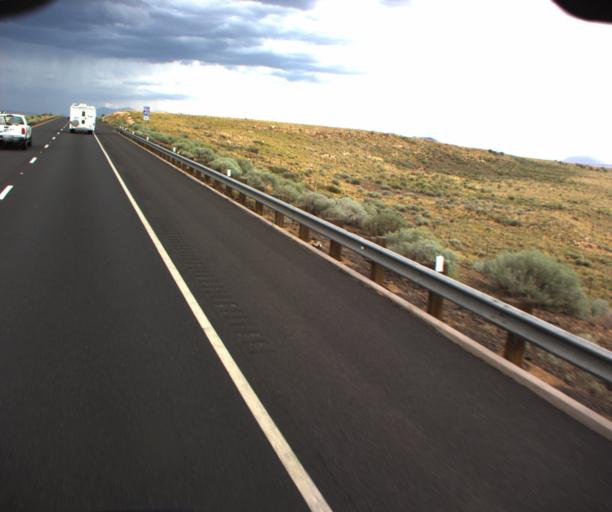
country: US
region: Arizona
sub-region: Coconino County
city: LeChee
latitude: 35.1324
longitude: -111.1923
